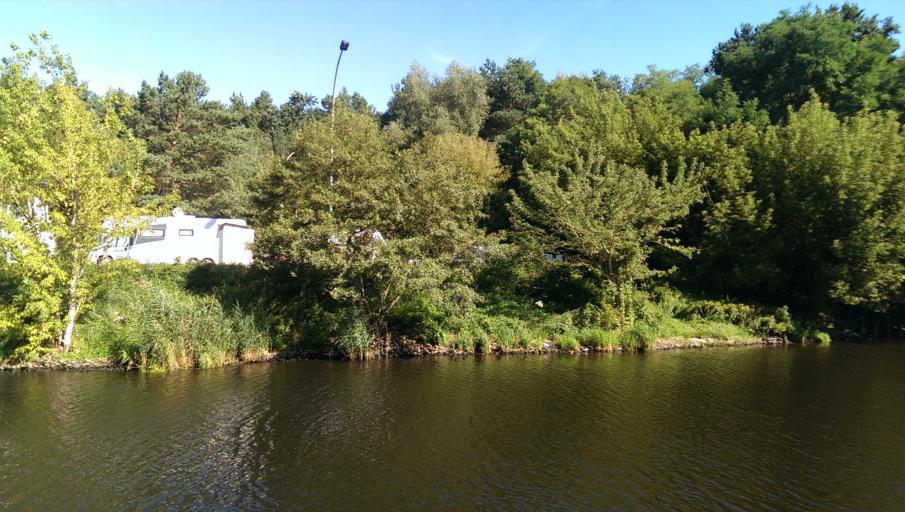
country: DE
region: Berlin
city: Wannsee
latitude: 52.3995
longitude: 13.1804
